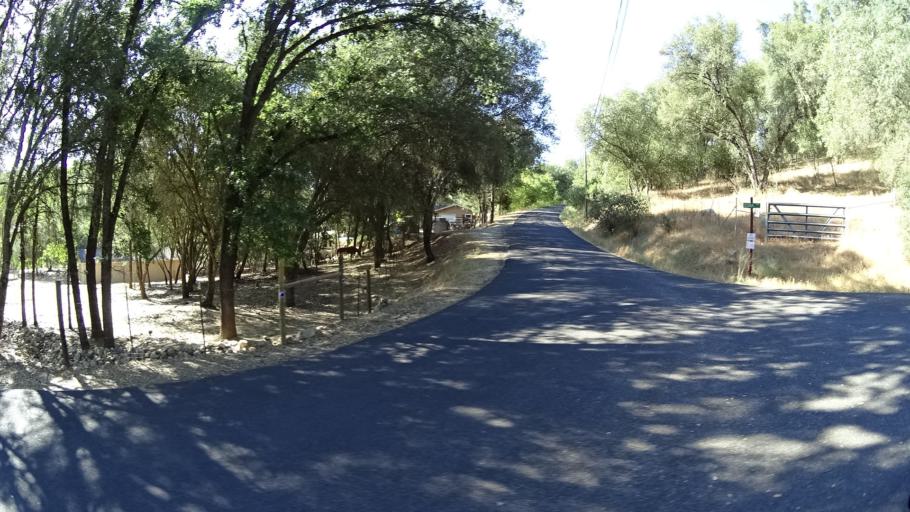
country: US
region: California
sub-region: Calaveras County
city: San Andreas
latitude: 38.2357
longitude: -120.7120
